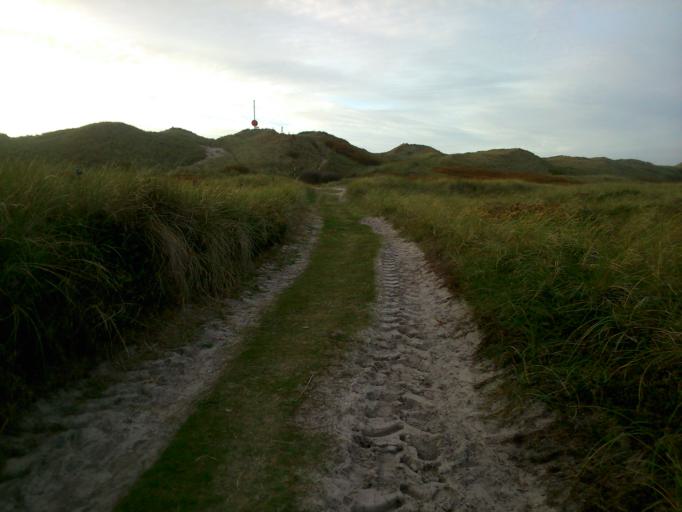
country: DK
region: Central Jutland
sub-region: Ringkobing-Skjern Kommune
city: Hvide Sande
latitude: 55.8413
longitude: 8.1670
